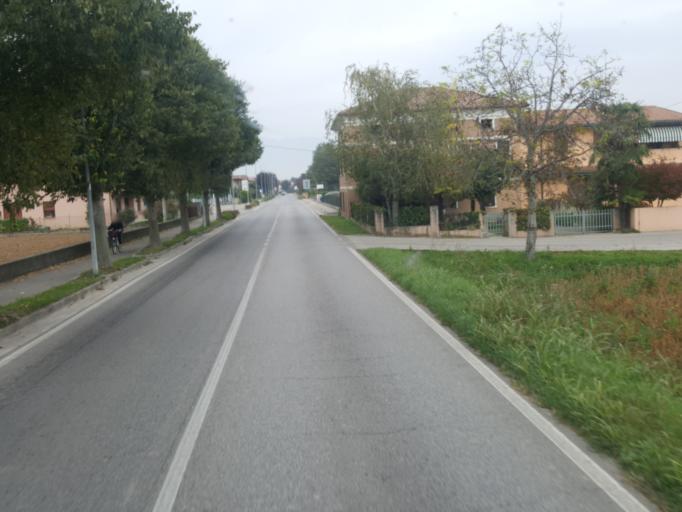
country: IT
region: Veneto
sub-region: Provincia di Treviso
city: Loria Bessica
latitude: 45.7221
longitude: 11.8667
